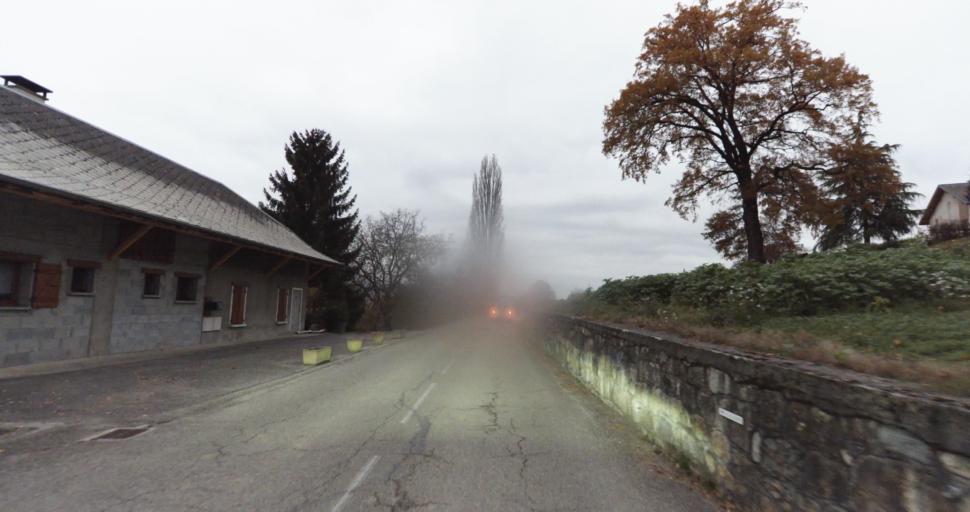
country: FR
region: Rhone-Alpes
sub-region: Departement de la Haute-Savoie
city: Alby-sur-Cheran
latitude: 45.8377
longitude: 6.0077
